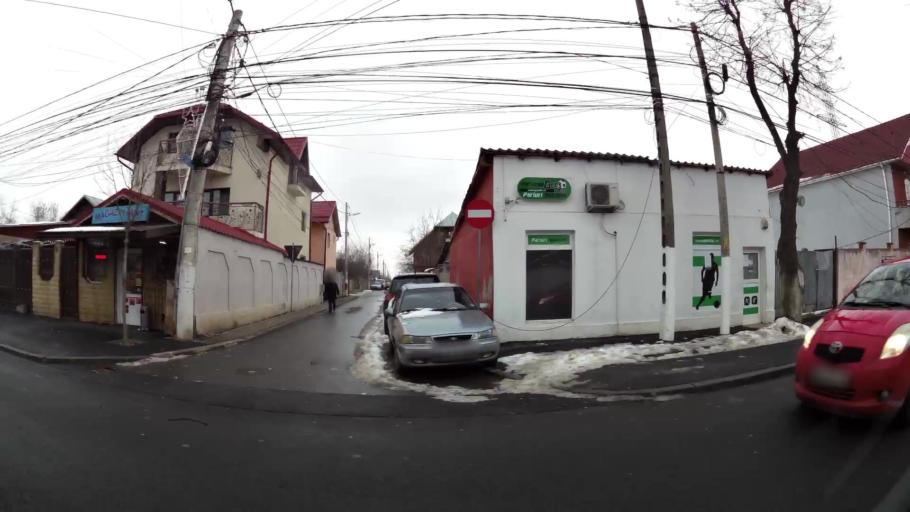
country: RO
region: Ilfov
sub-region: Comuna Pantelimon
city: Pantelimon
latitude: 44.4621
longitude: 26.2114
